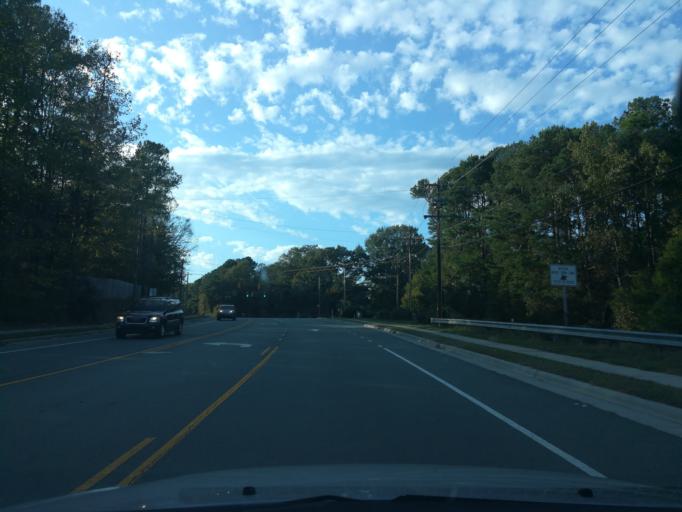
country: US
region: North Carolina
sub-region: Orange County
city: Chapel Hill
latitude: 35.9632
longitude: -79.0388
